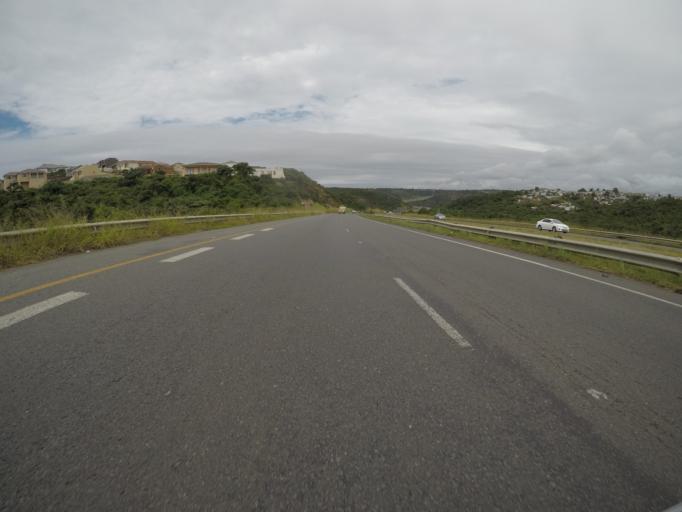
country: ZA
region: Eastern Cape
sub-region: Buffalo City Metropolitan Municipality
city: East London
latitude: -32.9579
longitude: 27.9284
